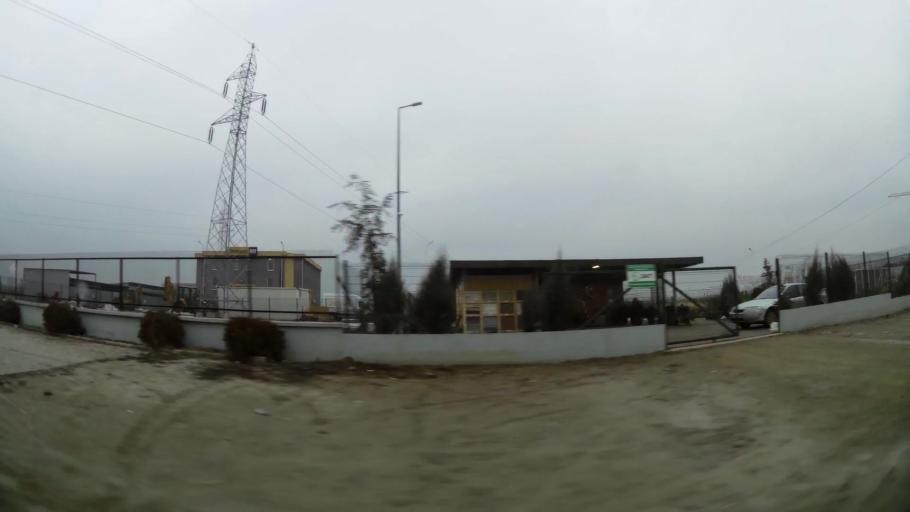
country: MK
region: Suto Orizari
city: Suto Orizare
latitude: 42.0471
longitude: 21.3864
